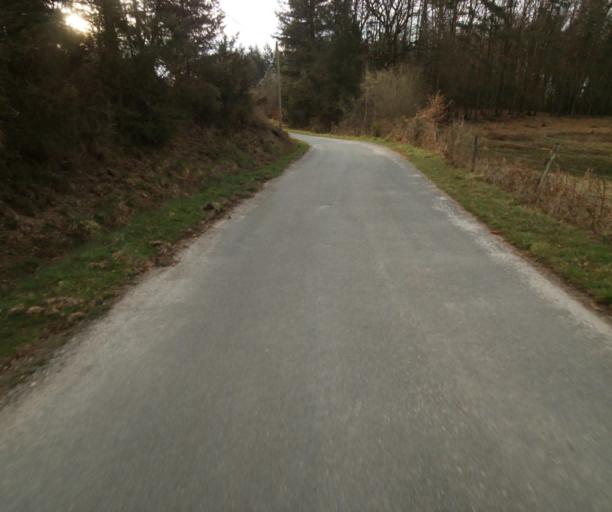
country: FR
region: Limousin
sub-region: Departement de la Correze
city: Correze
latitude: 45.4077
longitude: 1.9055
